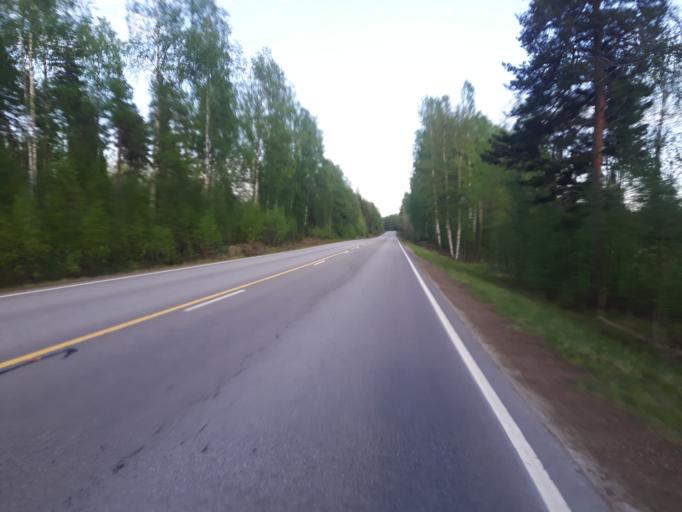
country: FI
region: Uusimaa
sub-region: Loviisa
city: Perna
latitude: 60.4605
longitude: 26.0481
